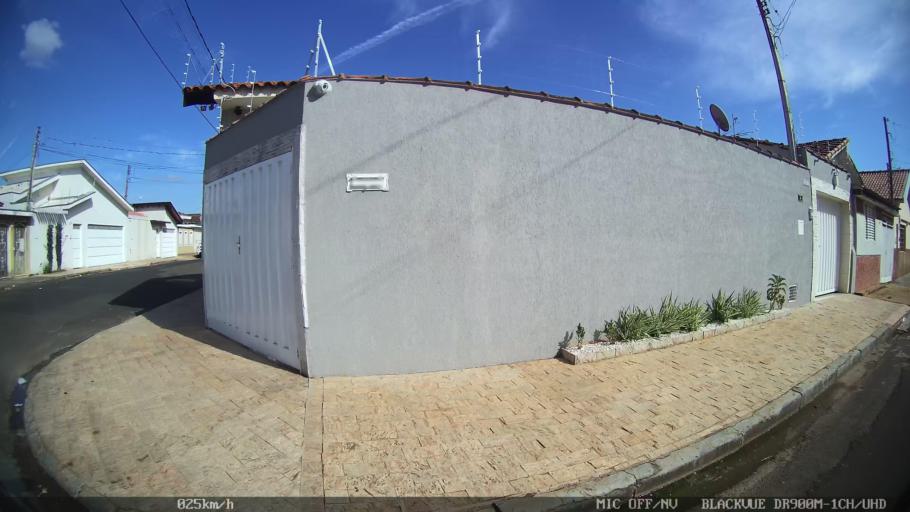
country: BR
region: Sao Paulo
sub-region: Franca
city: Franca
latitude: -20.5326
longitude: -47.4145
